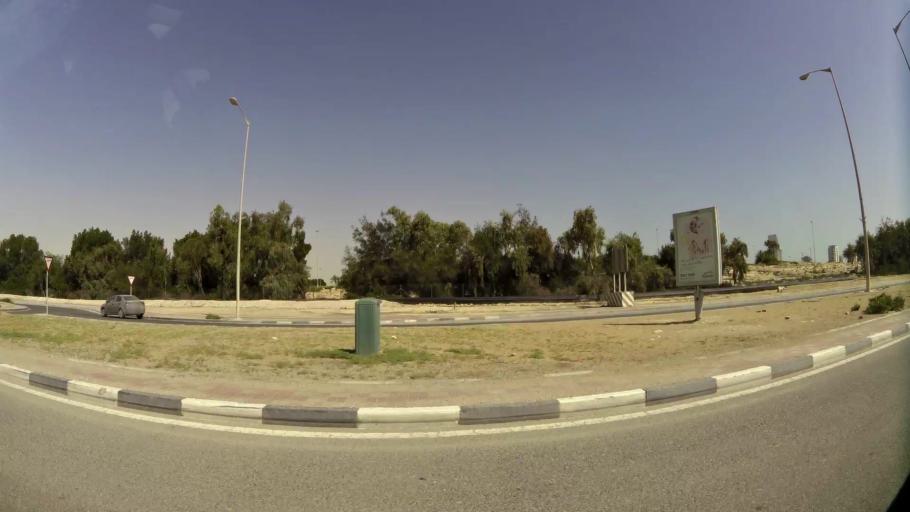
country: QA
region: Baladiyat ad Dawhah
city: Doha
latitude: 25.3773
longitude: 51.5092
